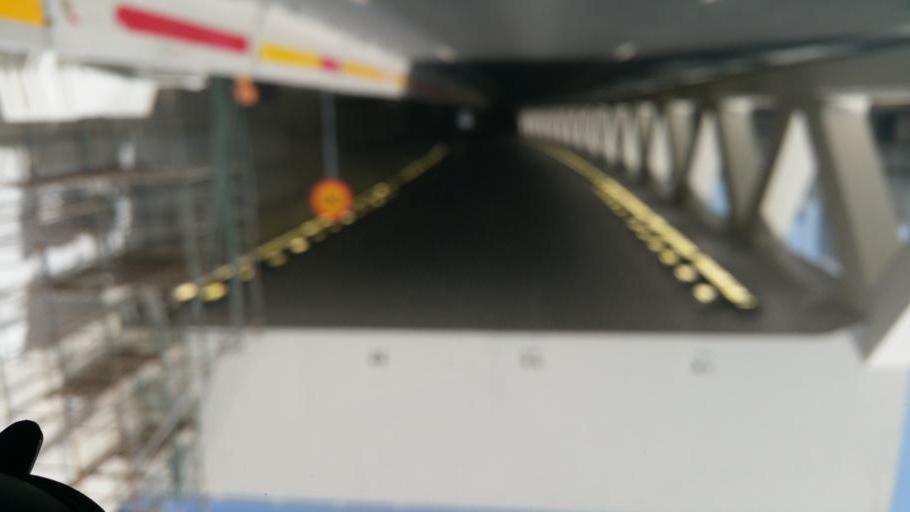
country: QA
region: Baladiyat Umm Salal
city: Umm Salal Muhammad
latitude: 25.4242
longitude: 51.5073
